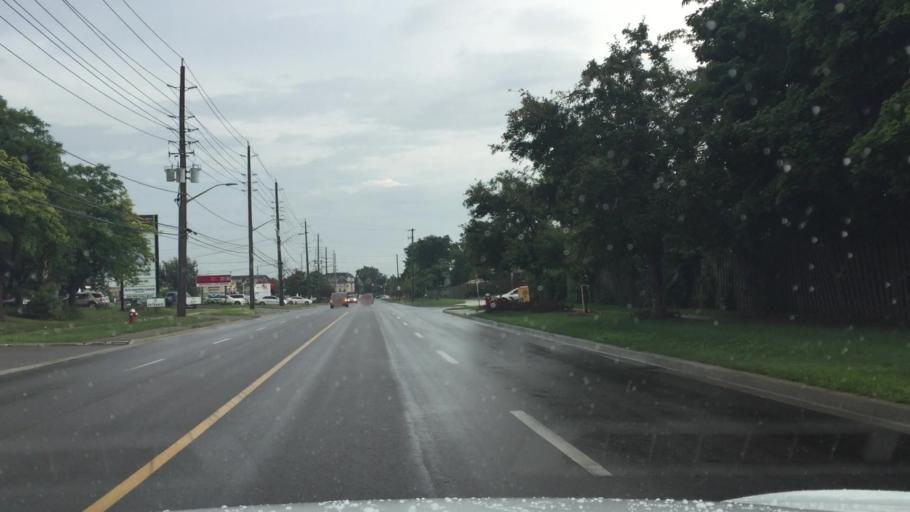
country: CA
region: Ontario
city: Mississauga
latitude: 43.5654
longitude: -79.6395
